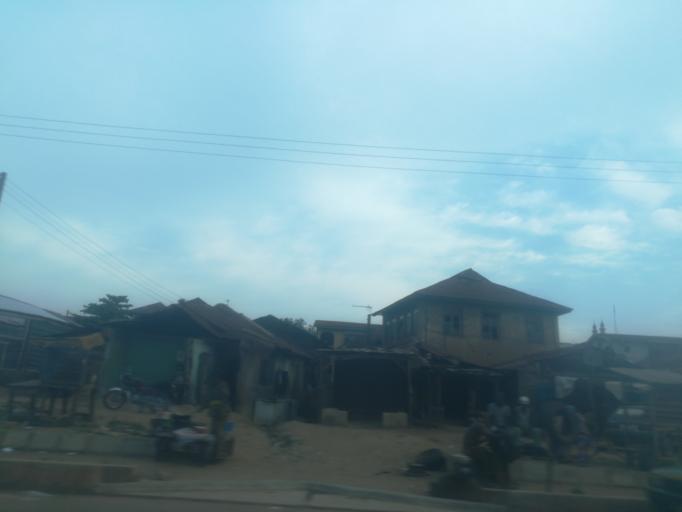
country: NG
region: Ogun
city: Abeokuta
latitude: 7.1638
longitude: 3.3336
